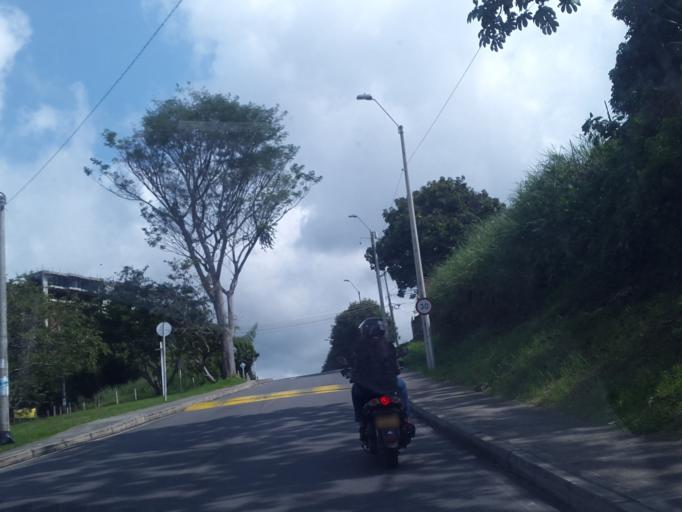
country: CO
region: Quindio
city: Calarca
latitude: 4.5559
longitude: -75.6583
